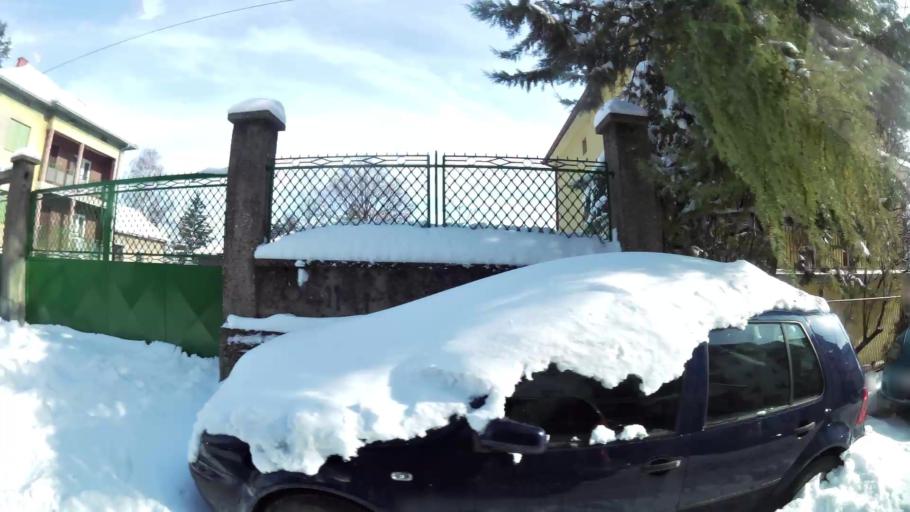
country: RS
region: Central Serbia
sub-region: Belgrade
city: Palilula
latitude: 44.7937
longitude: 20.5201
